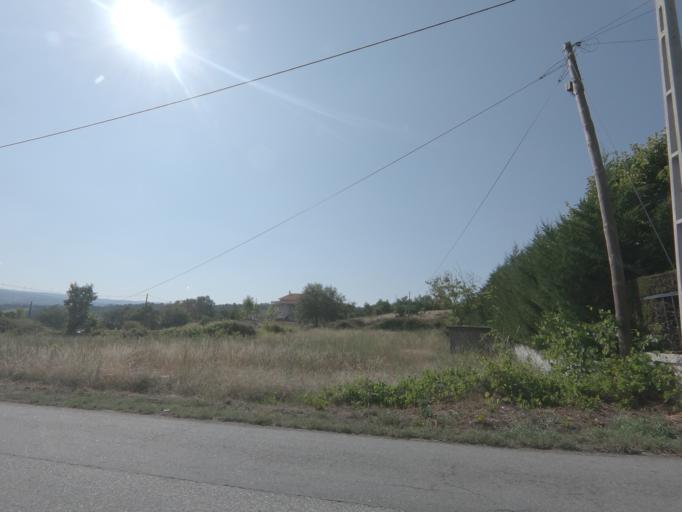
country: PT
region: Viseu
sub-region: Moimenta da Beira
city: Moimenta da Beira
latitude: 40.9880
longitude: -7.5631
